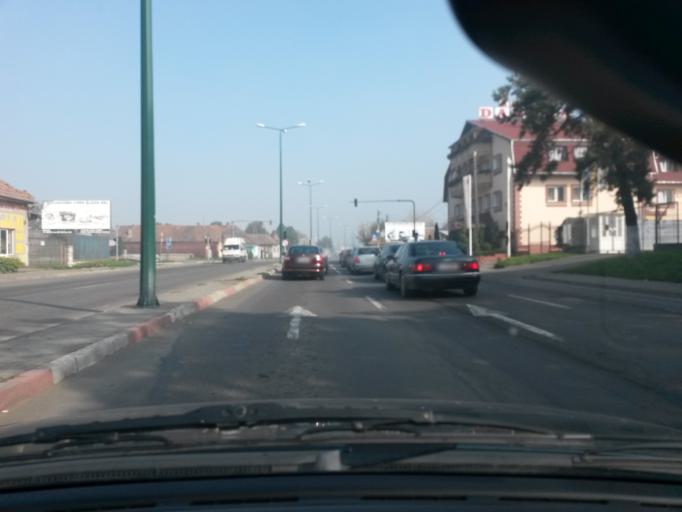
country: RO
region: Mures
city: Targu-Mures
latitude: 46.5256
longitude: 24.5390
